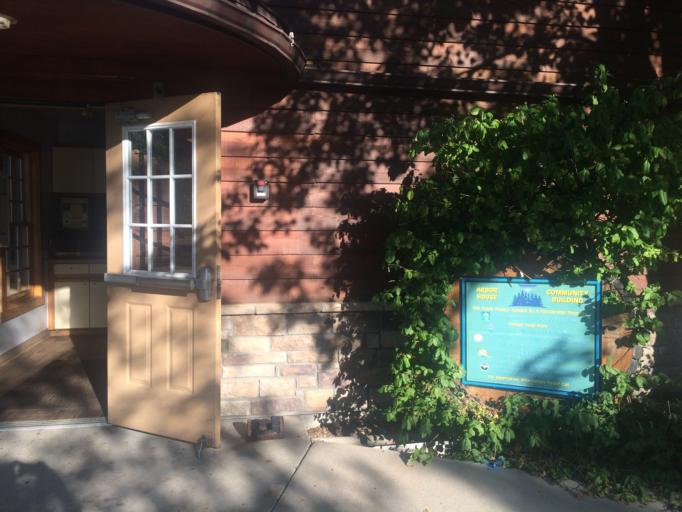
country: US
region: Colorado
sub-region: Jefferson County
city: Applewood
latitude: 39.7612
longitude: -105.1631
